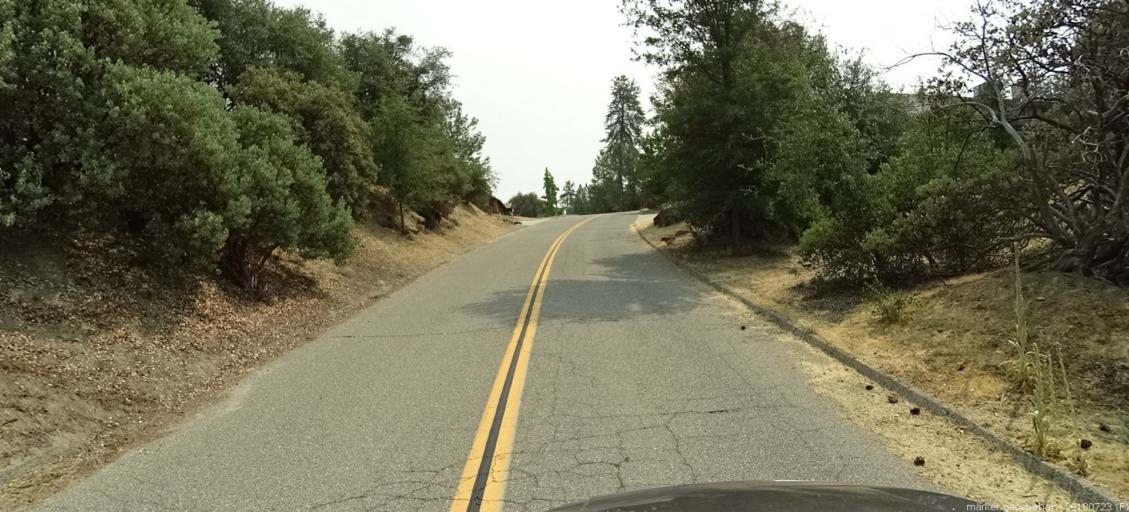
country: US
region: California
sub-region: Madera County
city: Ahwahnee
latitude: 37.3349
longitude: -119.7026
